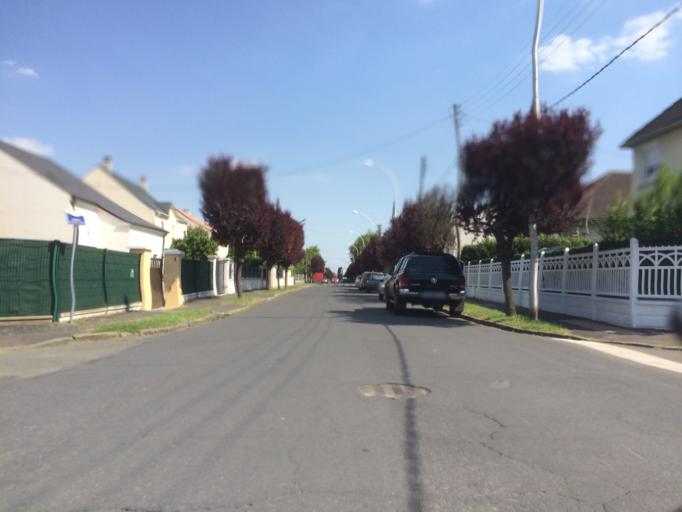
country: FR
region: Ile-de-France
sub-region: Departement de l'Essonne
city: Morangis
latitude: 48.6936
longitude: 2.3445
